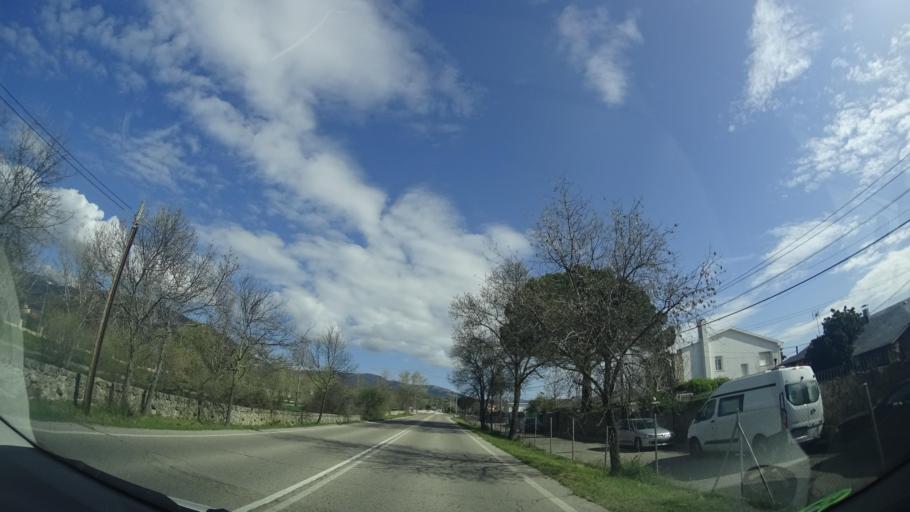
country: ES
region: Madrid
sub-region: Provincia de Madrid
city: Miraflores de la Sierra
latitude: 40.7631
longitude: -3.7819
